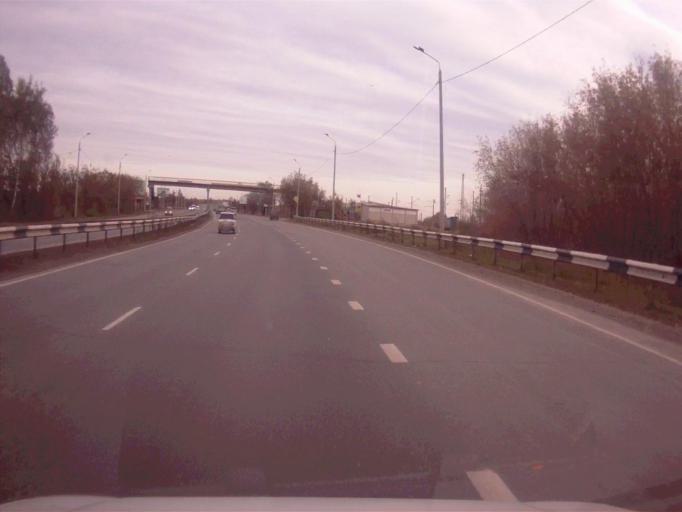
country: RU
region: Chelyabinsk
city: Novosineglazovskiy
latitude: 55.0430
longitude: 61.4256
